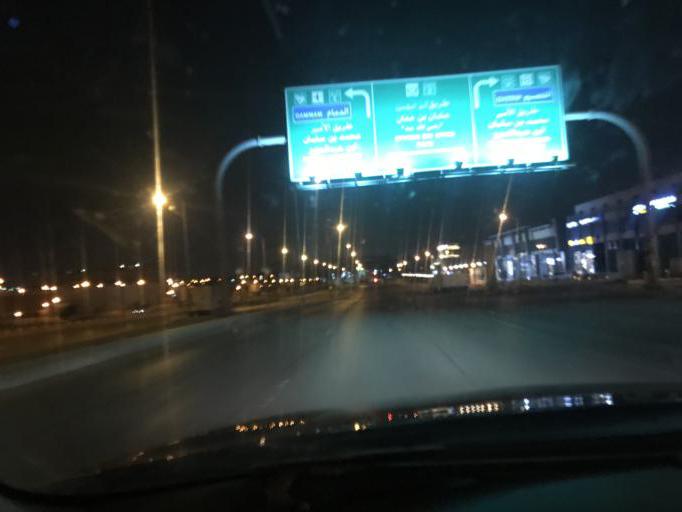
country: SA
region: Ar Riyad
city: Riyadh
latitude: 24.8061
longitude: 46.6936
